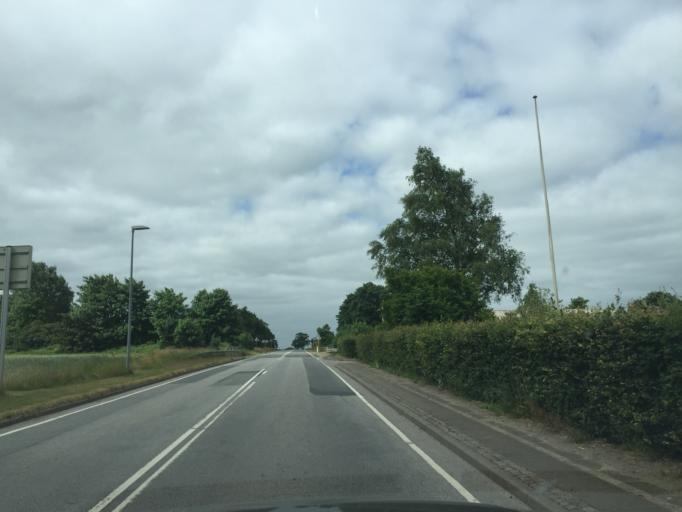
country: DK
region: South Denmark
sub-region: Vejen Kommune
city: Brorup
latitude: 55.4391
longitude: 8.9962
